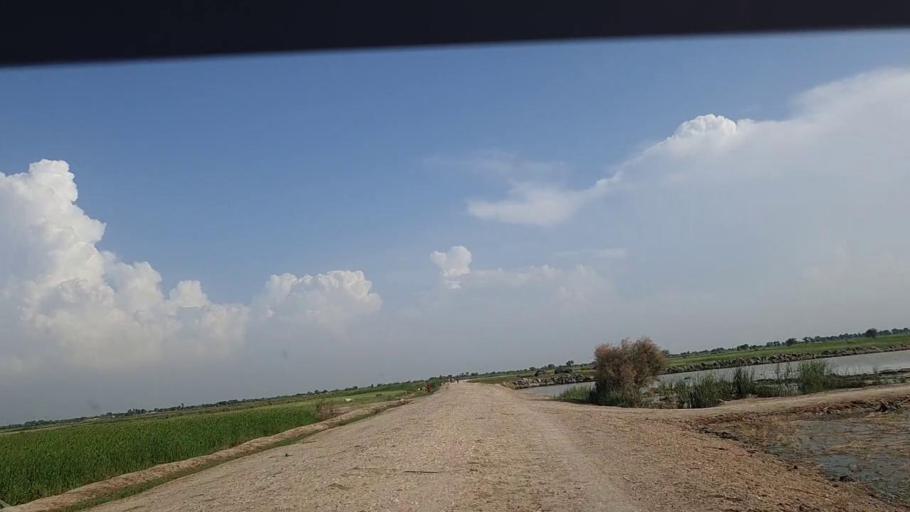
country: PK
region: Sindh
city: Khanpur
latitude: 27.8587
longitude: 69.3760
